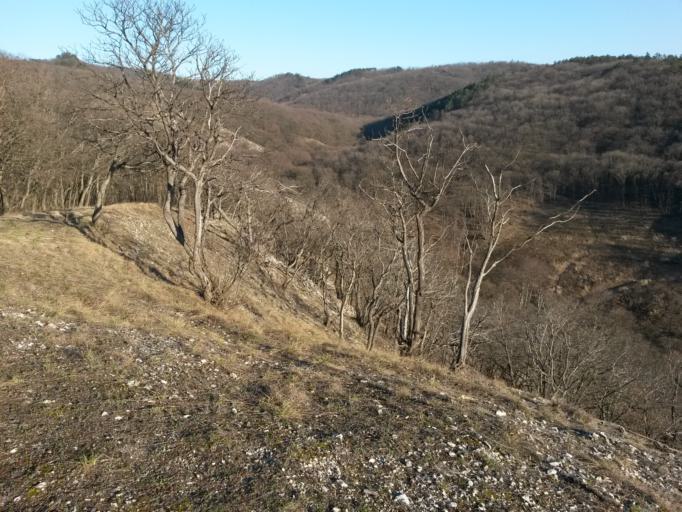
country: HU
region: Pest
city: Telki
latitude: 47.5874
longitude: 18.8194
